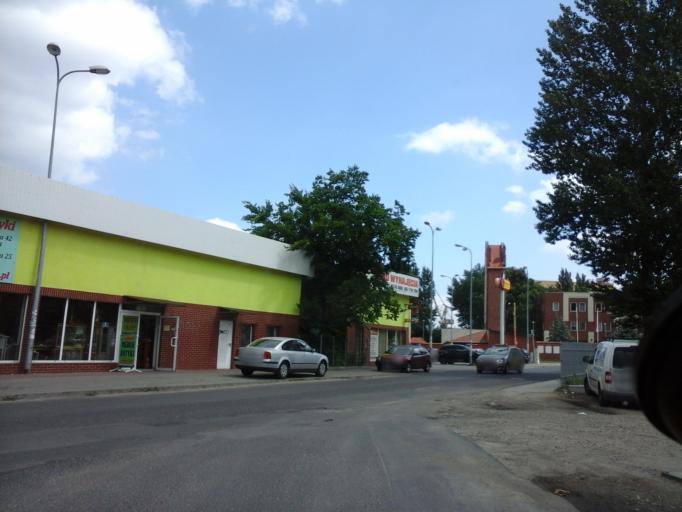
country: PL
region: West Pomeranian Voivodeship
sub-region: Szczecin
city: Szczecin
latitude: 53.4410
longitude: 14.5726
